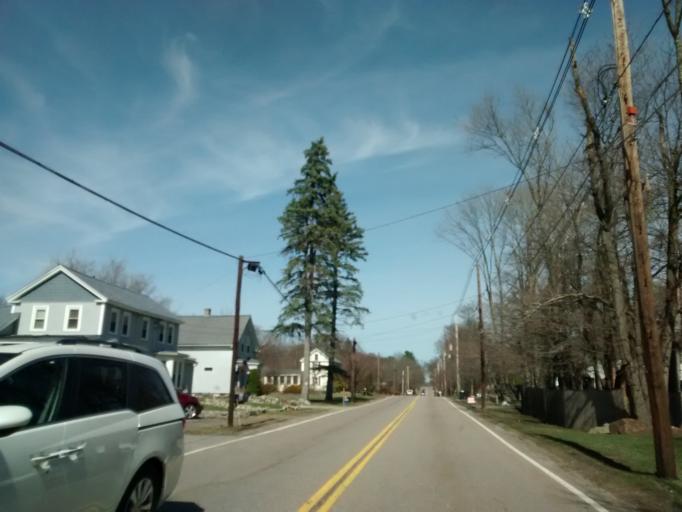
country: US
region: Massachusetts
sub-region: Norfolk County
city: Medway
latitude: 42.1377
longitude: -71.4415
